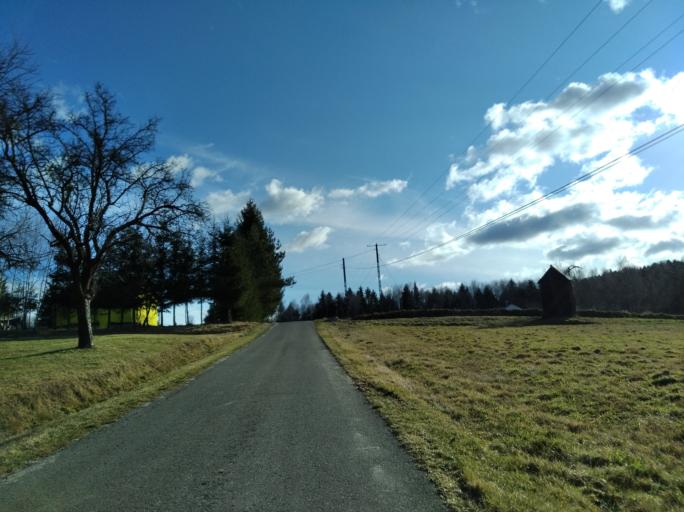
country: PL
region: Subcarpathian Voivodeship
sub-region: Powiat strzyzowski
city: Wisniowa
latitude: 49.8978
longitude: 21.6866
